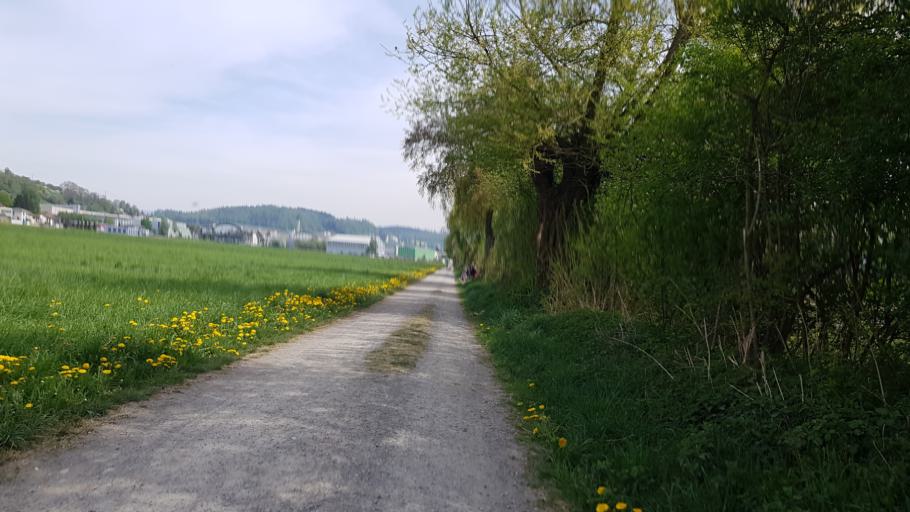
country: CH
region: Aargau
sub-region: Bezirk Kulm
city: Gontenschwil
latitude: 47.2719
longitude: 8.1608
